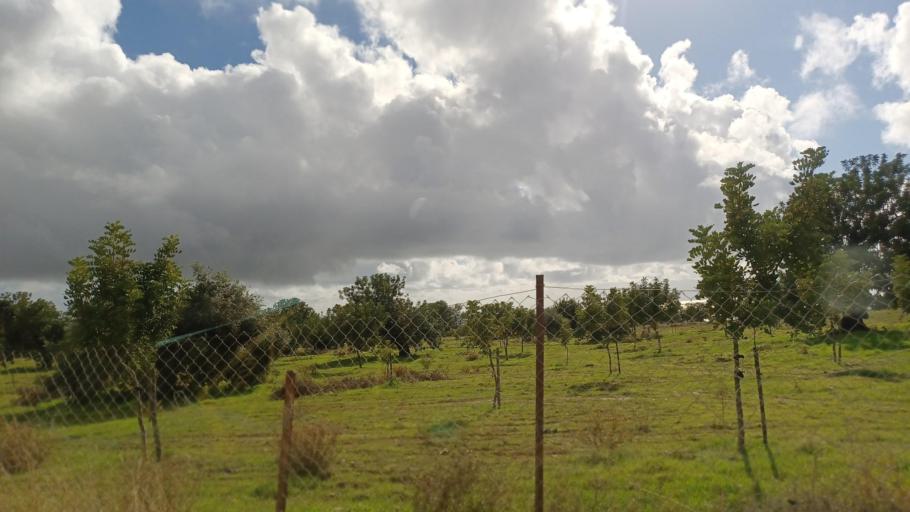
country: CY
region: Limassol
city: Sotira
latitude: 34.7239
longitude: 32.8278
